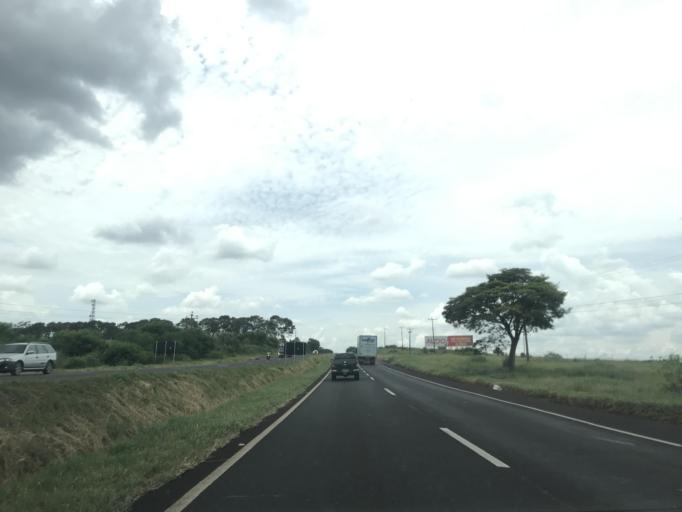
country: BR
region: Parana
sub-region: Paicandu
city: Paicandu
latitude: -23.3874
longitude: -52.0215
